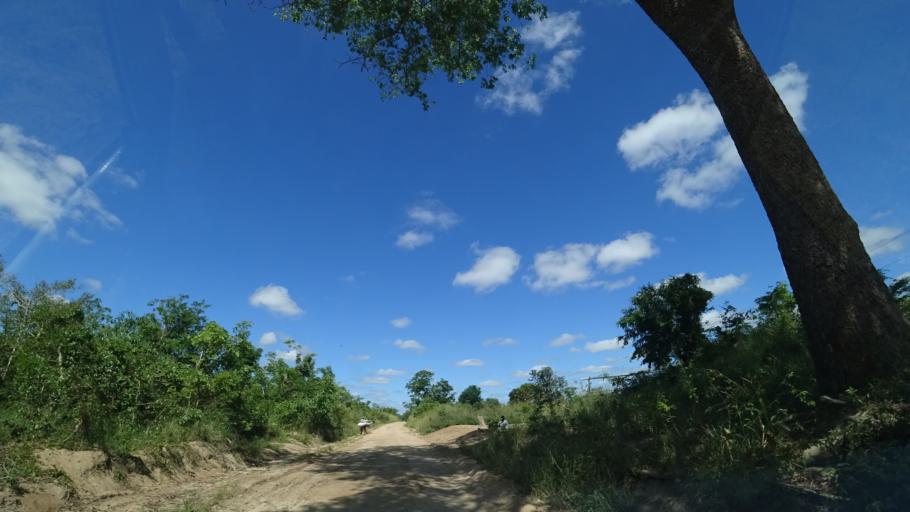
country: MZ
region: Sofala
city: Dondo
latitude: -19.3214
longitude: 34.6915
